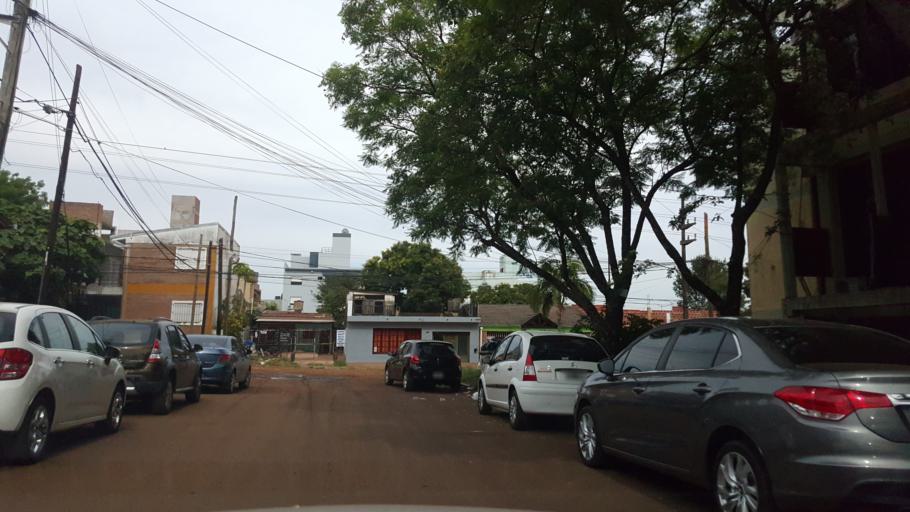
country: AR
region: Misiones
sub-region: Departamento de Capital
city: Posadas
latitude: -27.3587
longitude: -55.9055
